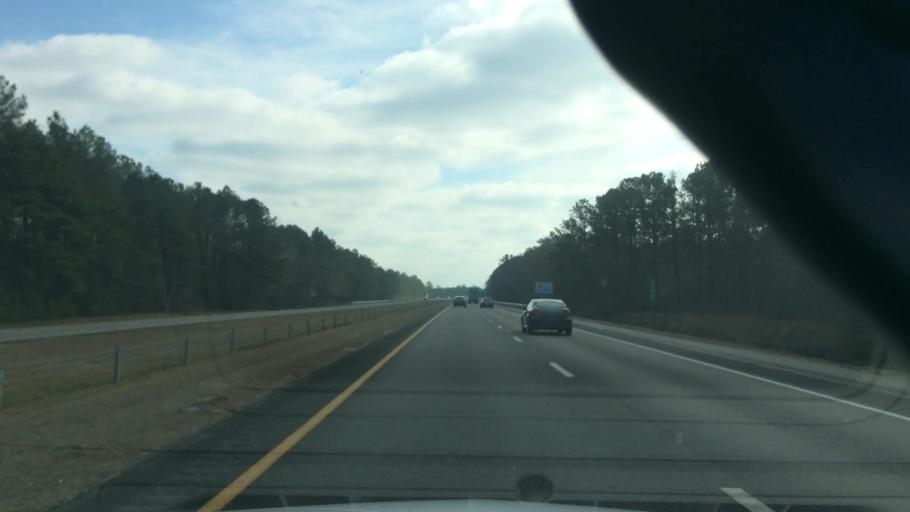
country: US
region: North Carolina
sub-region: Pender County
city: Burgaw
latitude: 34.5955
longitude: -77.9102
